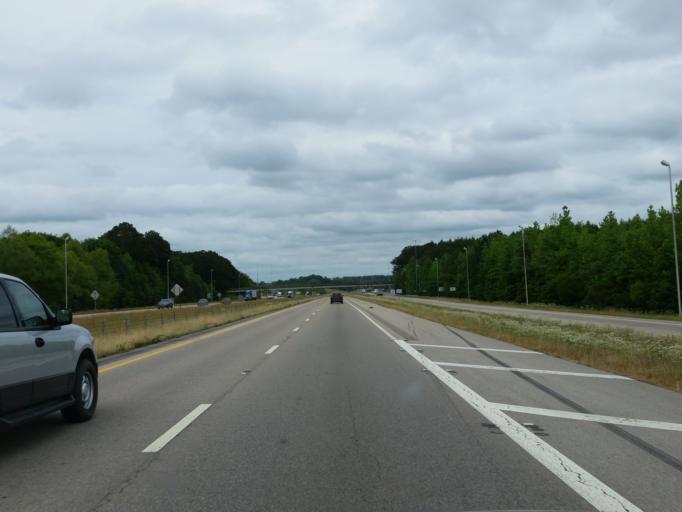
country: US
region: Alabama
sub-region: Sumter County
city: York
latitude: 32.4332
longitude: -88.4443
